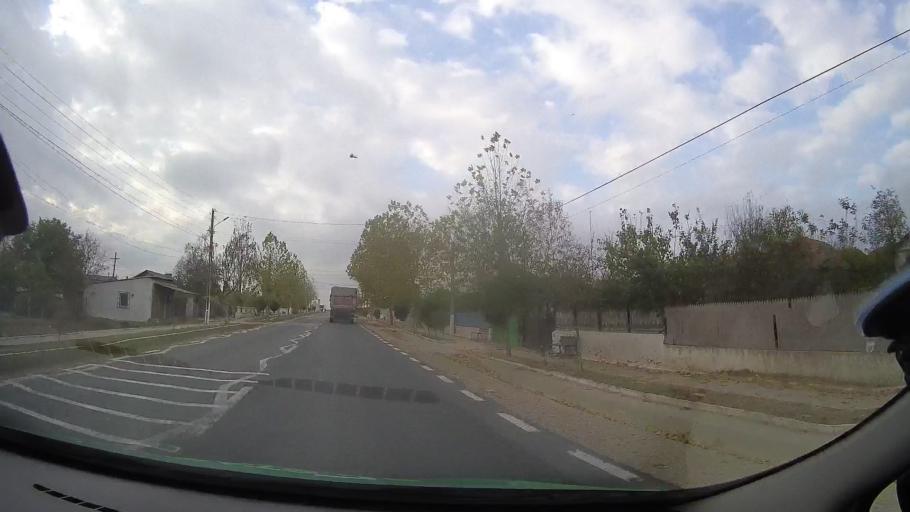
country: RO
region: Constanta
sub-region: Comuna Mircea Voda
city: Satu Nou
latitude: 44.2689
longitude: 28.2198
